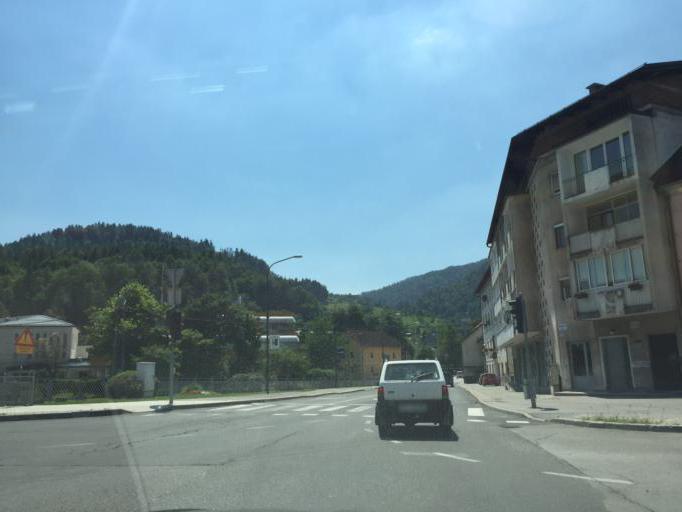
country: SI
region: Idrija
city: Idrija
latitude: 46.0031
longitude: 14.0279
